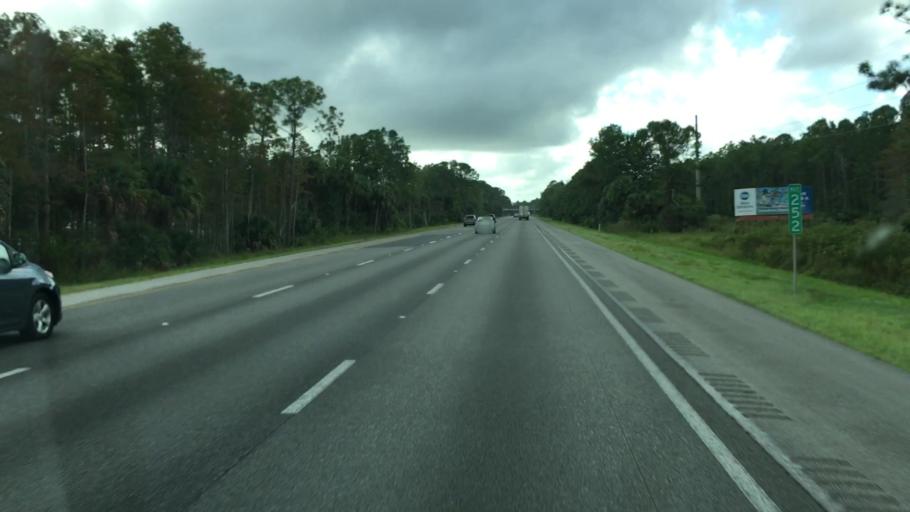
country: US
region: Florida
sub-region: Volusia County
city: Glencoe
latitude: 29.0556
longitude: -81.0080
